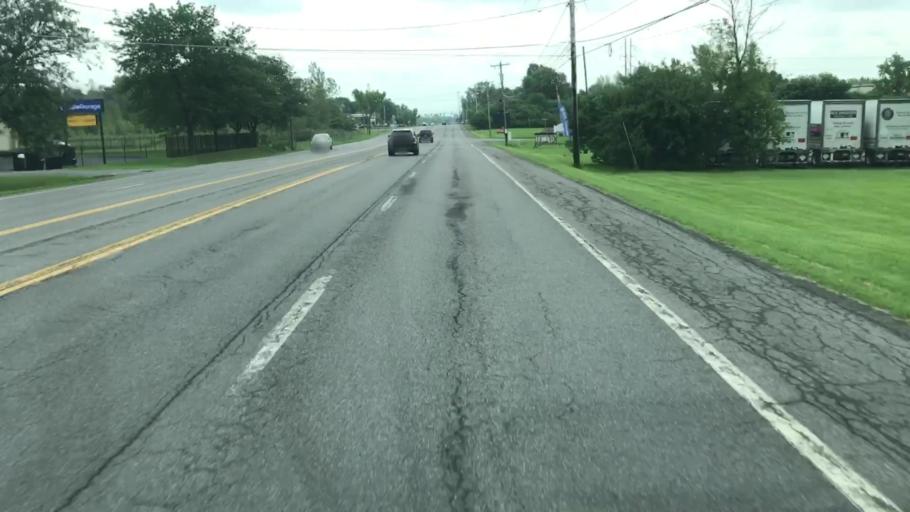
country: US
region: New York
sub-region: Onondaga County
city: Galeville
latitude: 43.1227
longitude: -76.1861
